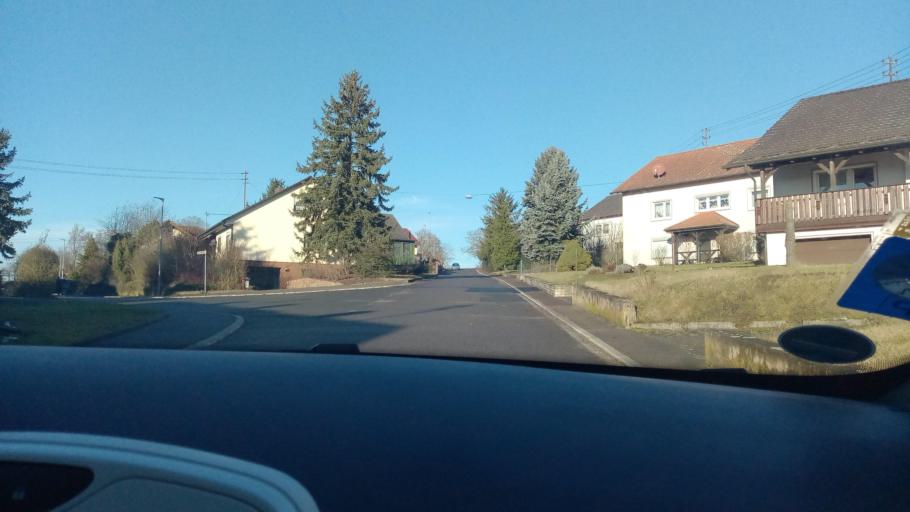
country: DE
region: Baden-Wuerttemberg
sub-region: Regierungsbezirk Stuttgart
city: Kulsheim
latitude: 49.6807
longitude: 9.5685
